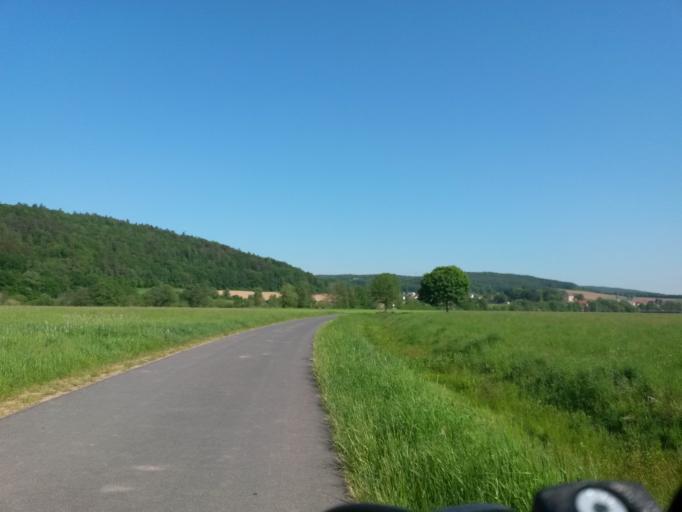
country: DE
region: Bavaria
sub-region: Regierungsbezirk Unterfranken
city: Bad Bocklet
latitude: 50.2447
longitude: 10.0623
